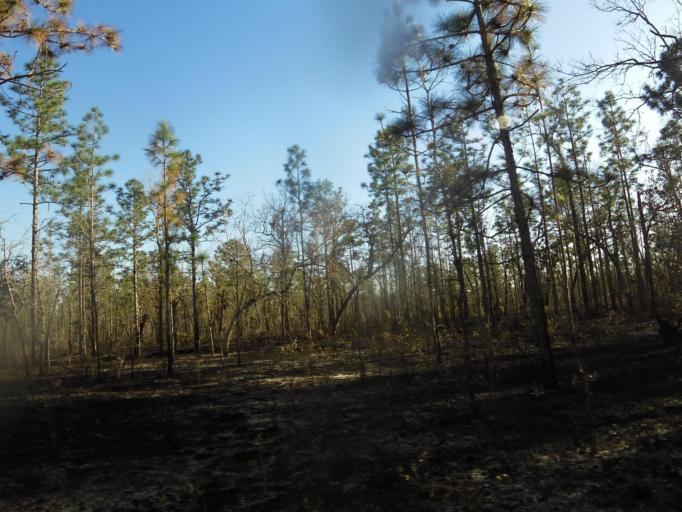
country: US
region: Florida
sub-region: Clay County
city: Middleburg
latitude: 30.1309
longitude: -81.9007
